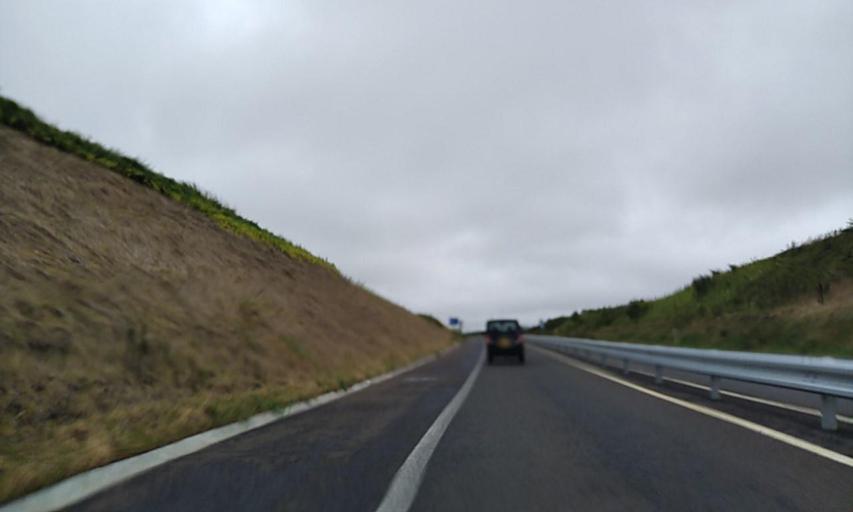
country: JP
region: Hokkaido
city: Nemuro
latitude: 43.3129
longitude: 145.5471
